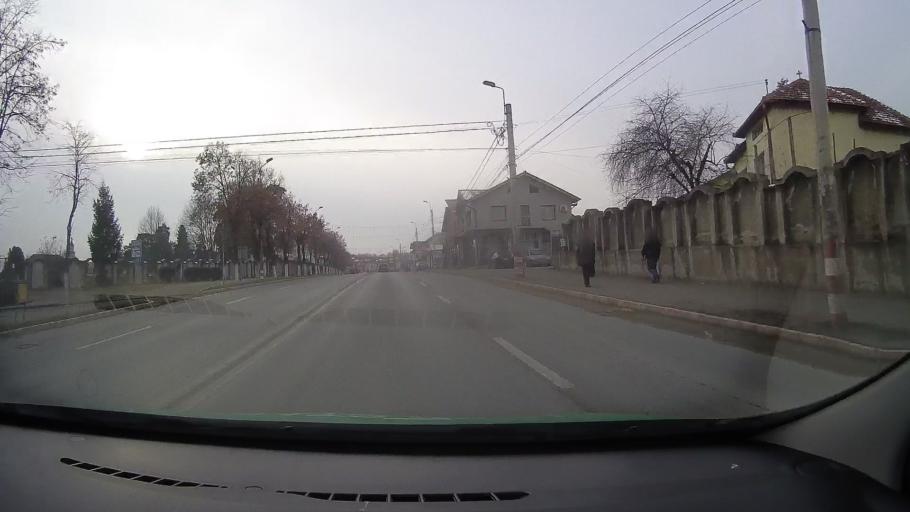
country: RO
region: Hunedoara
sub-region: Municipiul Orastie
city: Orastie
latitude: 45.8411
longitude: 23.1944
